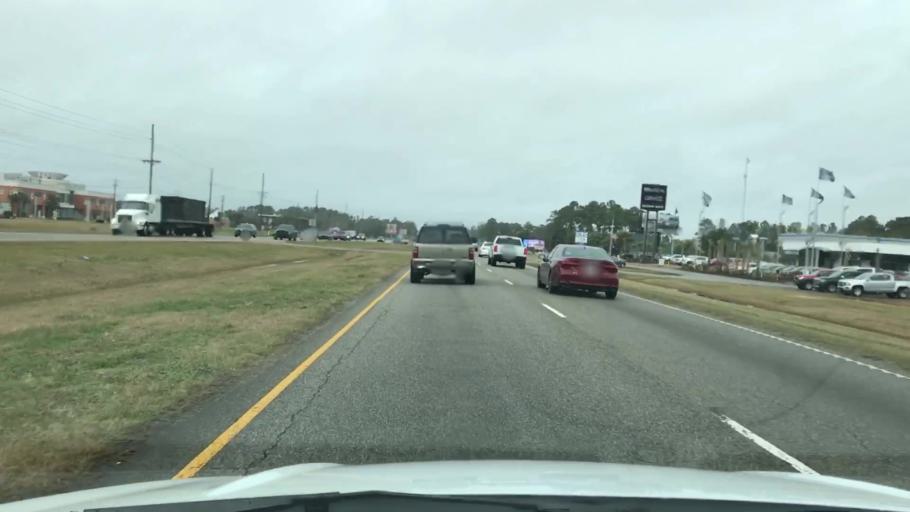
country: US
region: South Carolina
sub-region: Horry County
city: Red Hill
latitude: 33.7930
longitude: -78.9988
